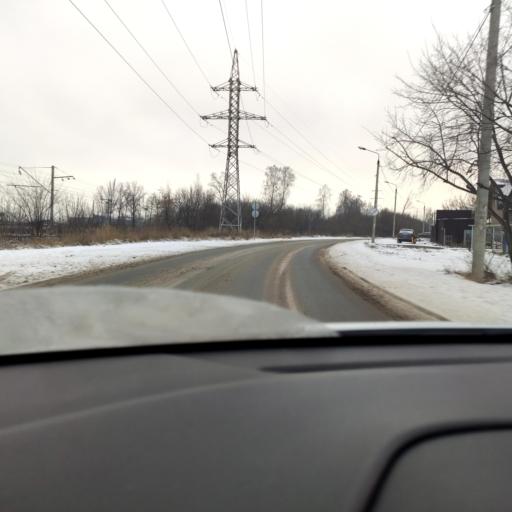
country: RU
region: Tatarstan
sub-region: Gorod Kazan'
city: Kazan
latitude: 55.8323
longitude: 49.1912
